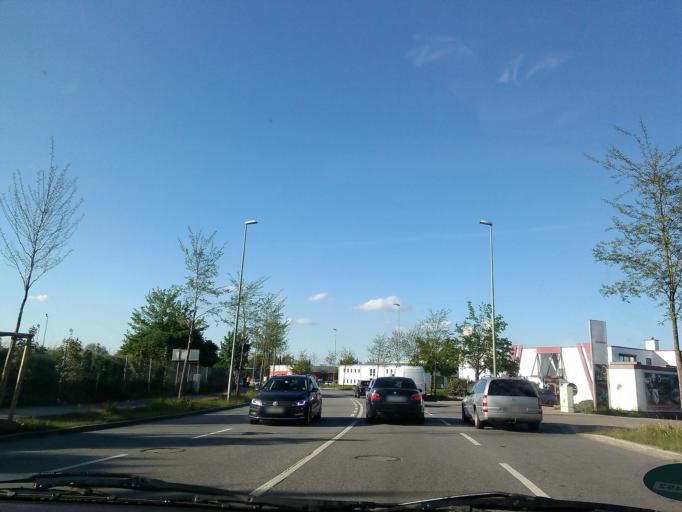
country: DE
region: Bavaria
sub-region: Swabia
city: Augsburg
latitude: 48.3851
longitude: 10.9382
